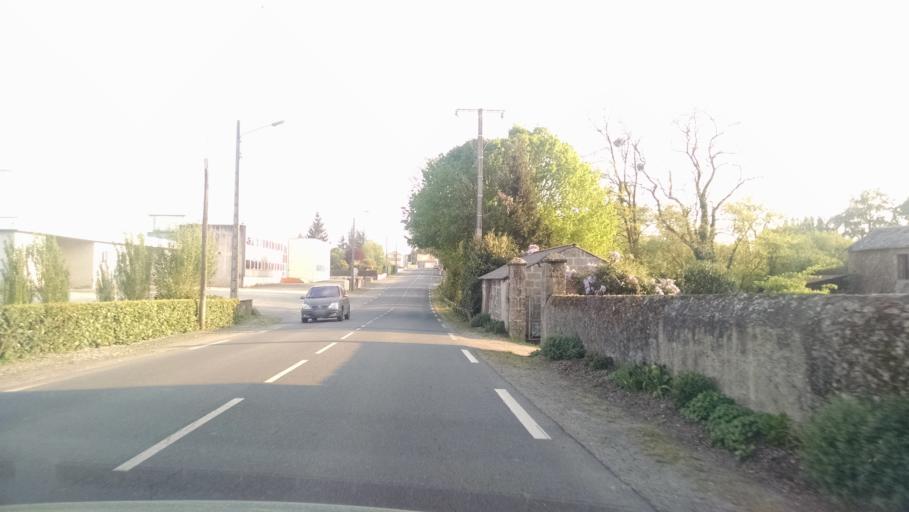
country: FR
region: Pays de la Loire
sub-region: Departement de la Loire-Atlantique
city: Boussay
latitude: 47.0535
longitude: -1.1842
